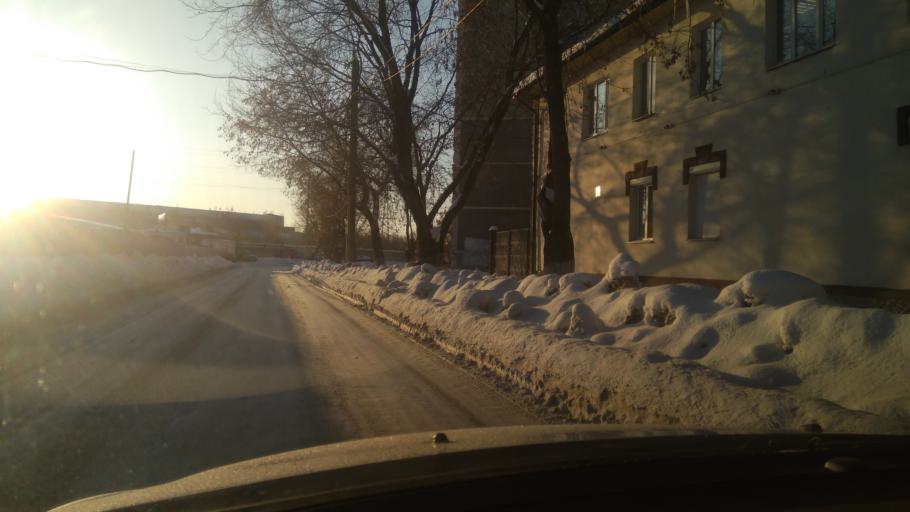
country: RU
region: Sverdlovsk
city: Yekaterinburg
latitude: 56.8818
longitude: 60.5671
